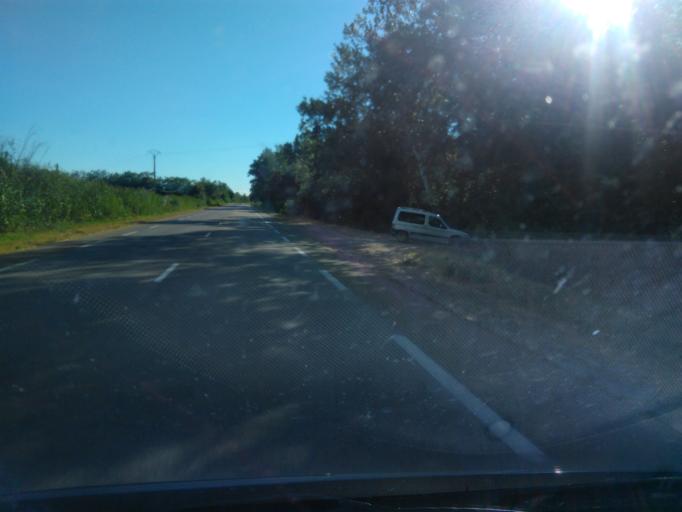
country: FR
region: Languedoc-Roussillon
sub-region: Departement du Gard
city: Saint-Gilles
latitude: 43.6722
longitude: 4.4805
